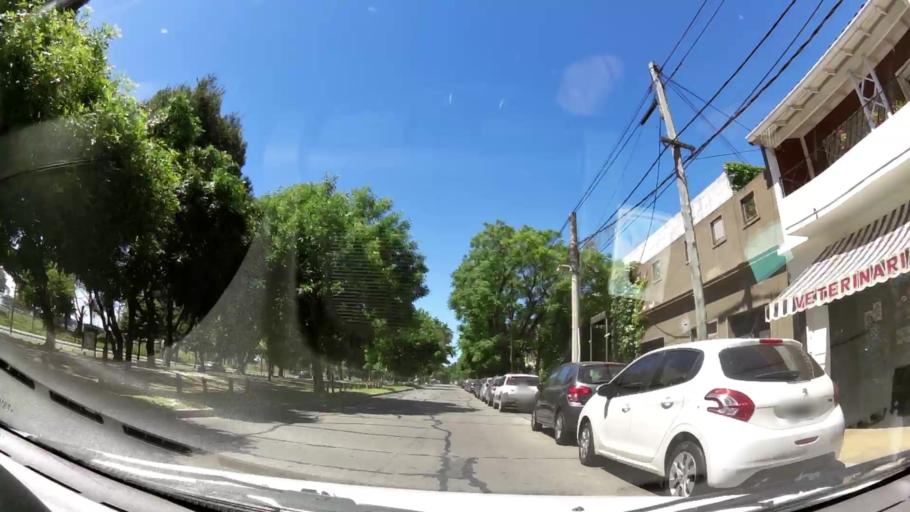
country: AR
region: Buenos Aires
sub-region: Partido de San Isidro
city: San Isidro
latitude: -34.4887
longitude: -58.5225
